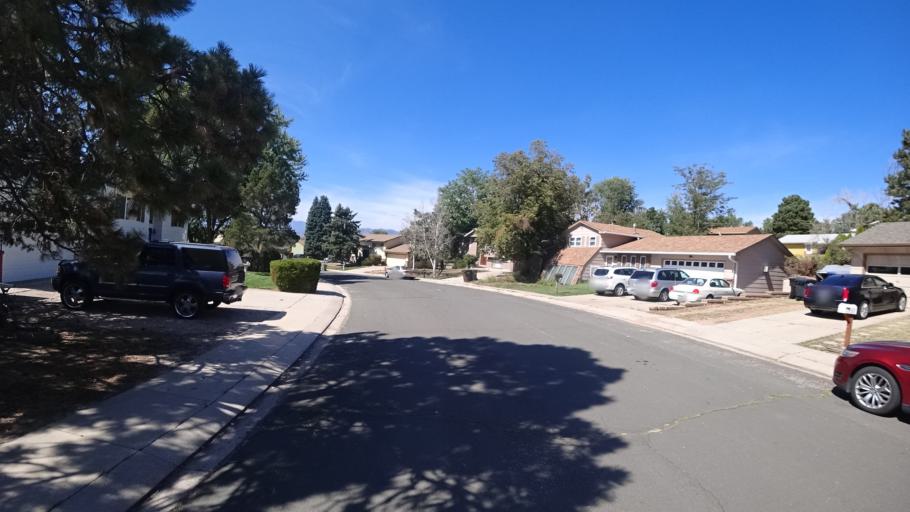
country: US
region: Colorado
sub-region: El Paso County
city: Cimarron Hills
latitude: 38.9060
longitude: -104.7665
